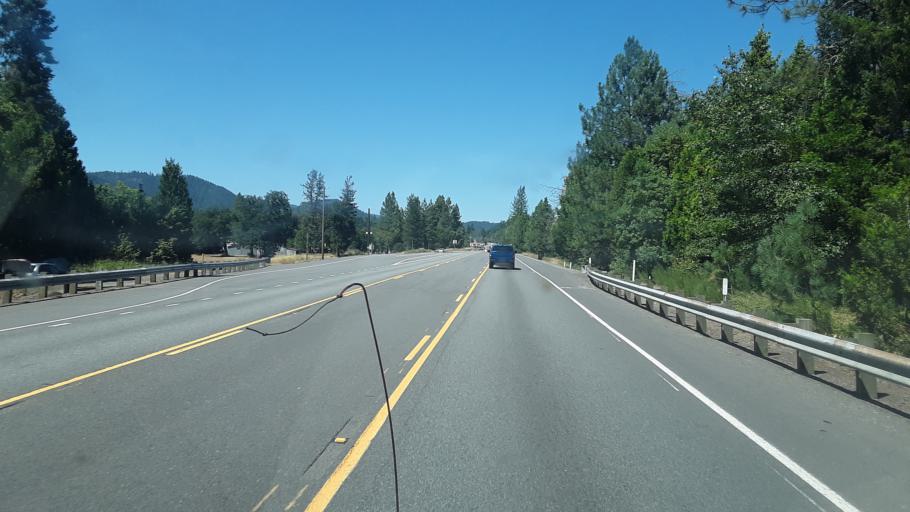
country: US
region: Oregon
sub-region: Josephine County
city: Cave Junction
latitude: 42.2718
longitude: -123.6188
